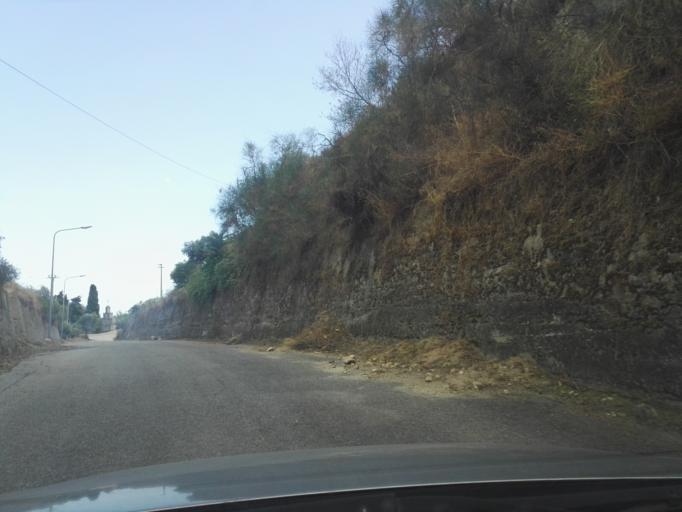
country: IT
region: Calabria
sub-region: Provincia di Reggio Calabria
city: Riace
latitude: 38.4155
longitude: 16.4817
